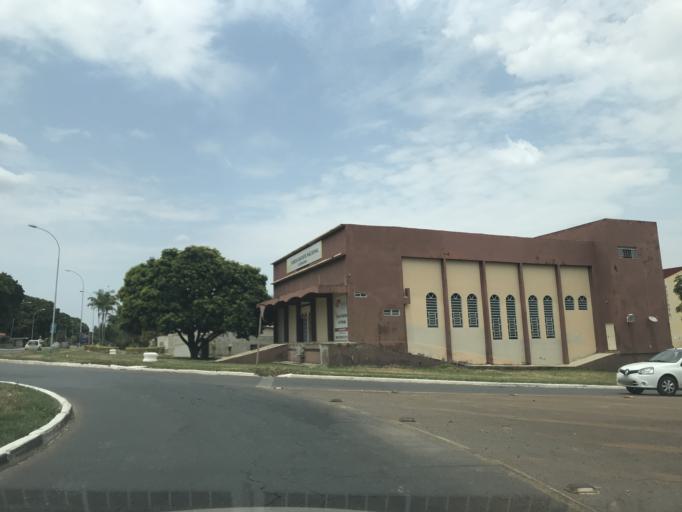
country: BR
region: Federal District
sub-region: Brasilia
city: Brasilia
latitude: -15.6518
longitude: -47.8042
